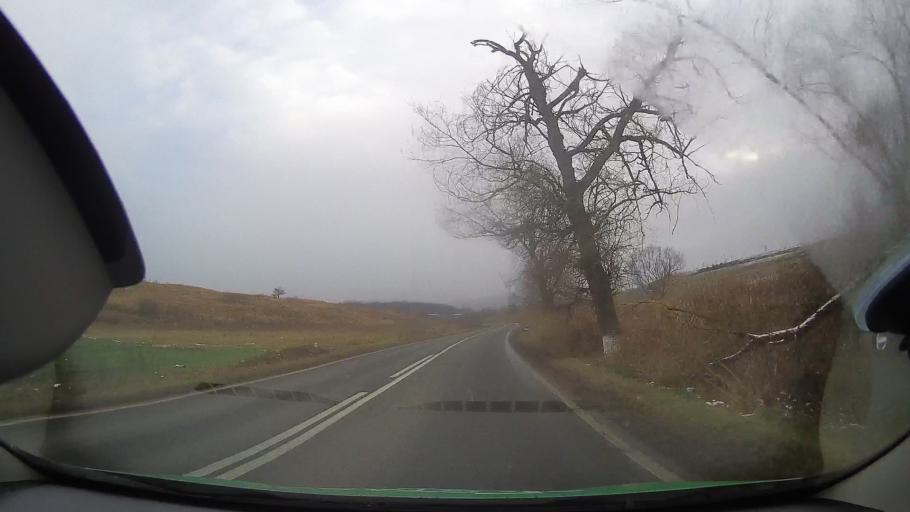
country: RO
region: Sibiu
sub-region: Comuna Blajel
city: Blajel
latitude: 46.2325
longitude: 24.3097
